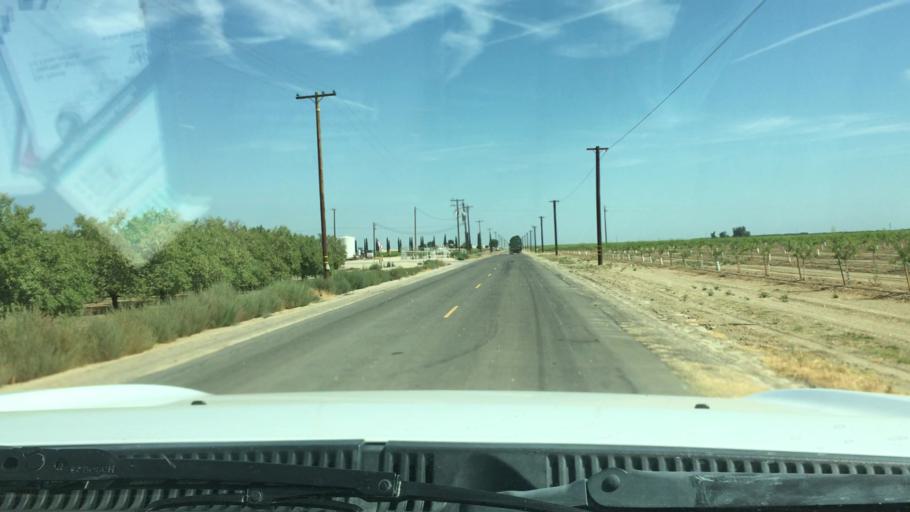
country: US
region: California
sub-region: Kern County
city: Shafter
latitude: 35.4547
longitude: -119.3681
